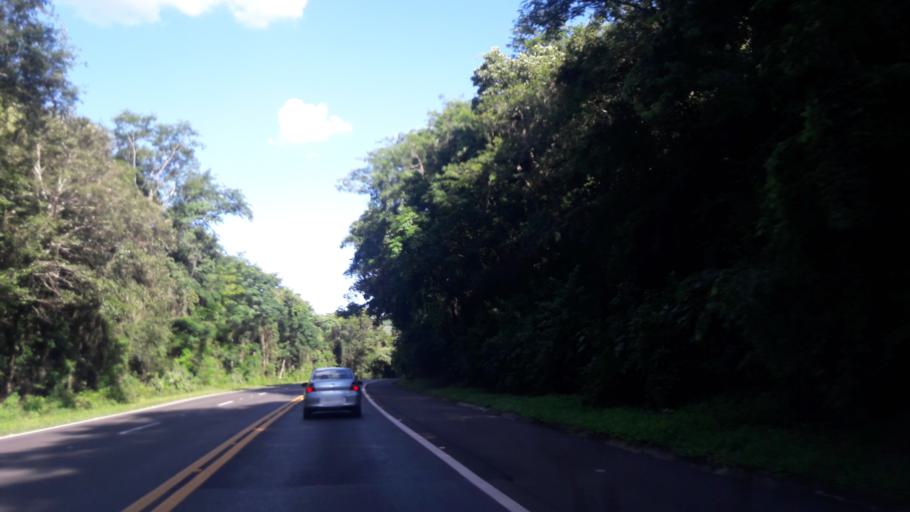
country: BR
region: Parana
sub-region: Laranjeiras Do Sul
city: Laranjeiras do Sul
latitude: -25.4156
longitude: -52.0740
